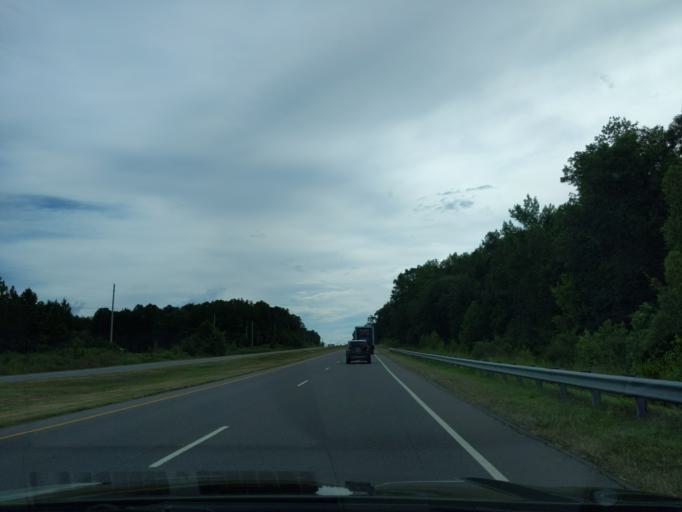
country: US
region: North Carolina
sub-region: Cabarrus County
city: Mount Pleasant
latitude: 35.3980
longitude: -80.4740
